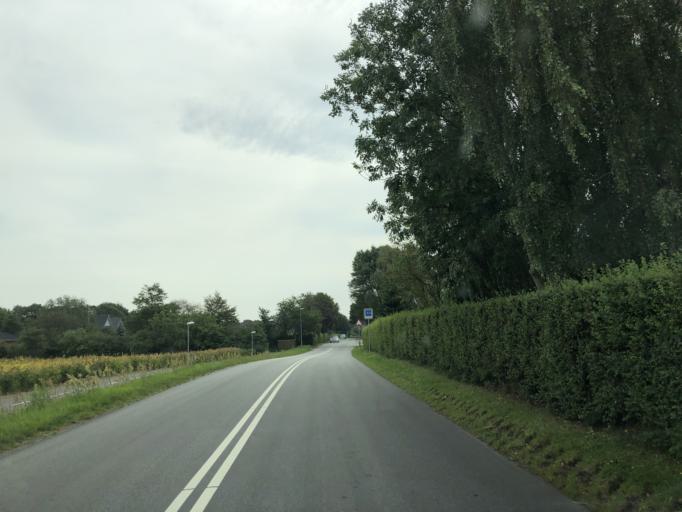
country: DK
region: Central Jutland
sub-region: Viborg Kommune
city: Stoholm
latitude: 56.4488
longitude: 9.1814
